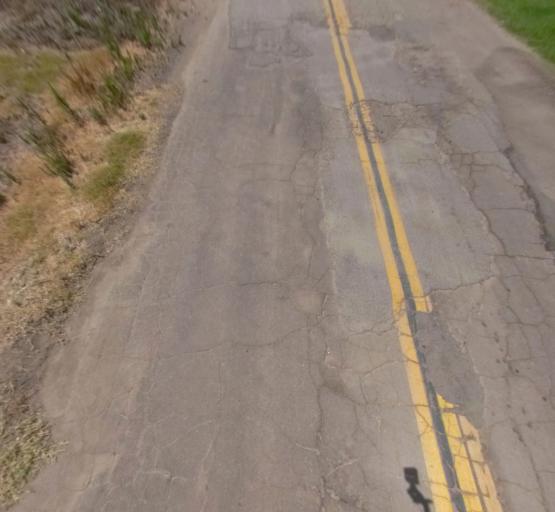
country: US
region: California
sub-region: Madera County
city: Chowchilla
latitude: 37.0985
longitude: -120.4553
